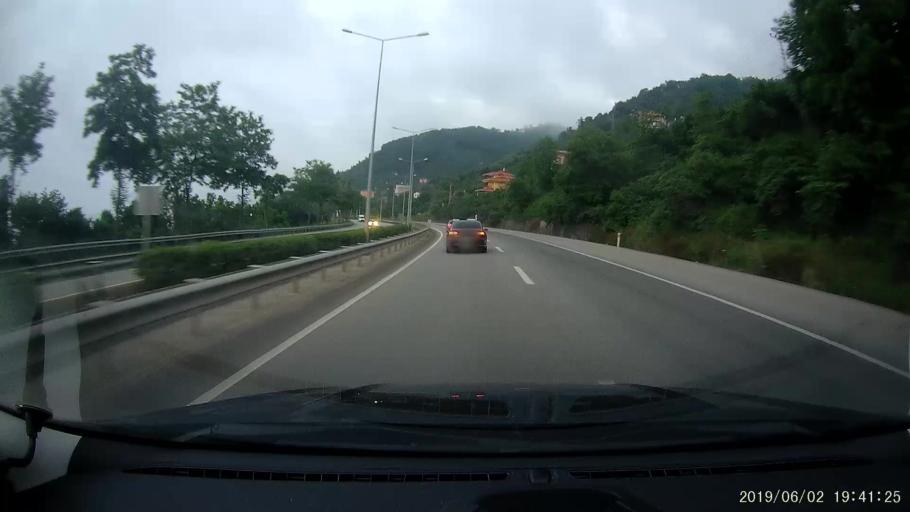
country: TR
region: Giresun
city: Kesap
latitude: 40.9138
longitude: 38.4797
